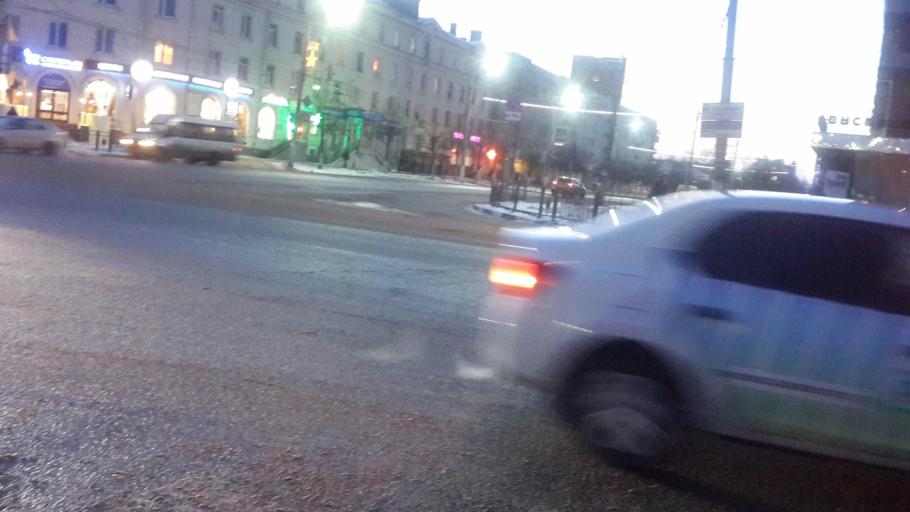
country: RU
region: Tula
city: Tula
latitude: 54.1973
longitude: 37.6013
